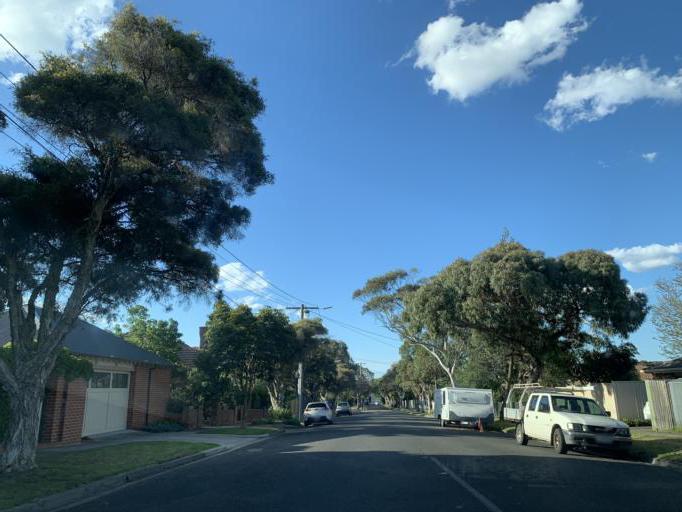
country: AU
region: Victoria
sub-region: Bayside
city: Hampton
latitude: -37.9400
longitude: 145.0075
